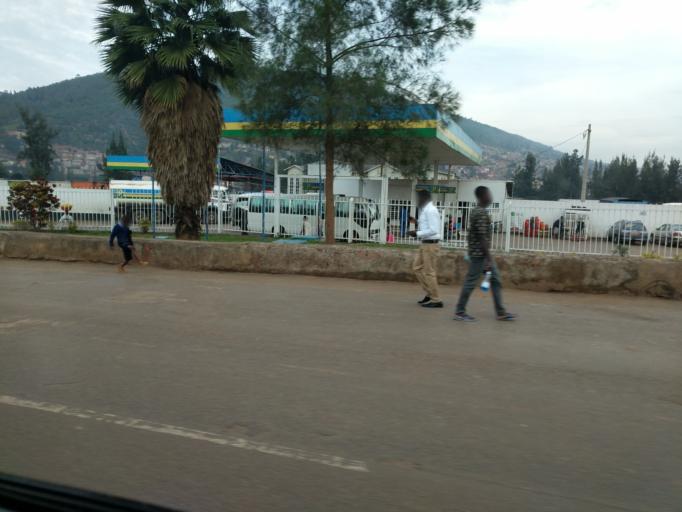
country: RW
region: Kigali
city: Kigali
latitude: -1.9397
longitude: 30.0510
